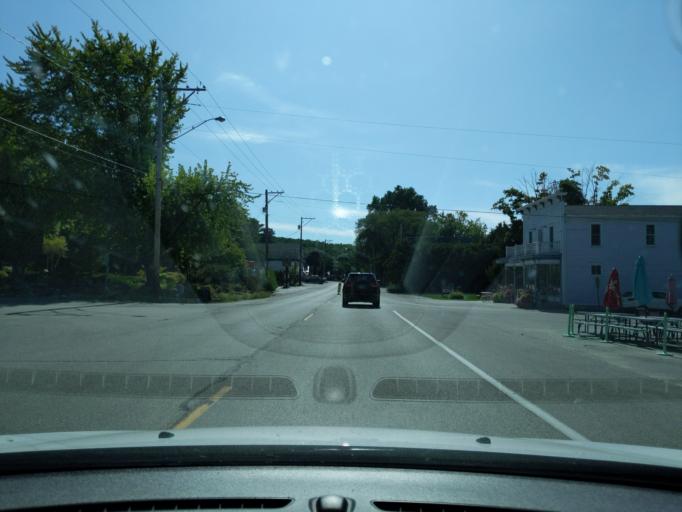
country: US
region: Michigan
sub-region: Delta County
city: Escanaba
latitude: 45.2541
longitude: -87.0731
